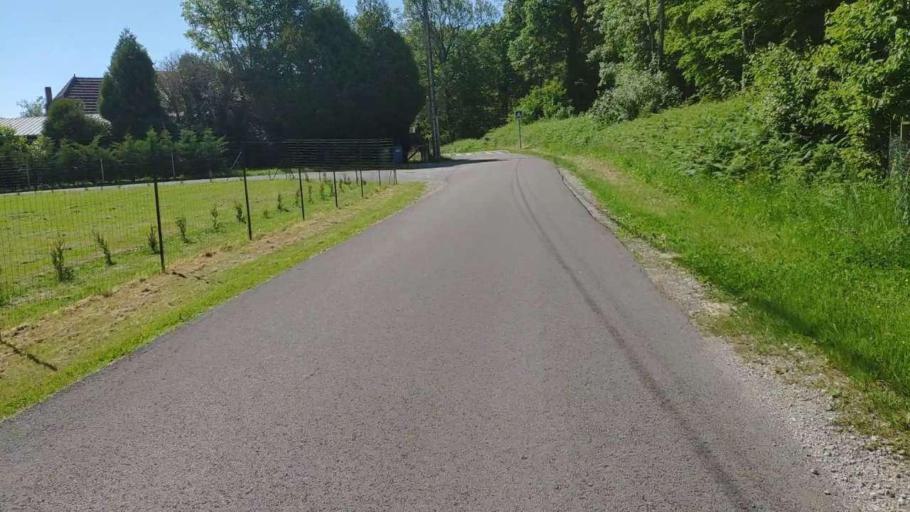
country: FR
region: Franche-Comte
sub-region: Departement du Jura
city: Bletterans
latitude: 46.7982
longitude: 5.4459
